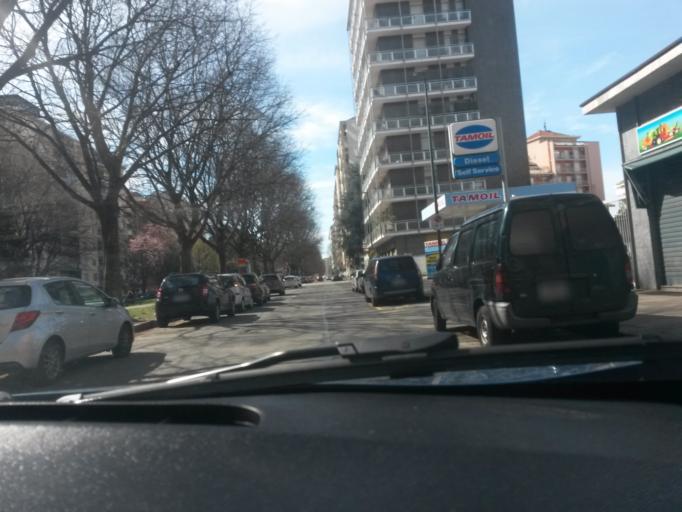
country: IT
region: Piedmont
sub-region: Provincia di Torino
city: Lesna
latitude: 45.0811
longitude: 7.6277
